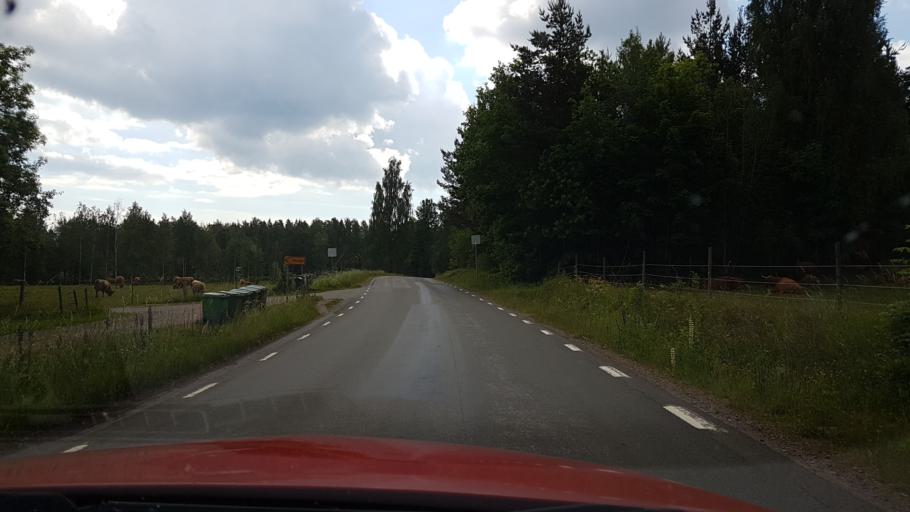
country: SE
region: Vaestra Goetaland
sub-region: Tibro Kommun
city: Tibro
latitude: 58.3129
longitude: 14.1757
